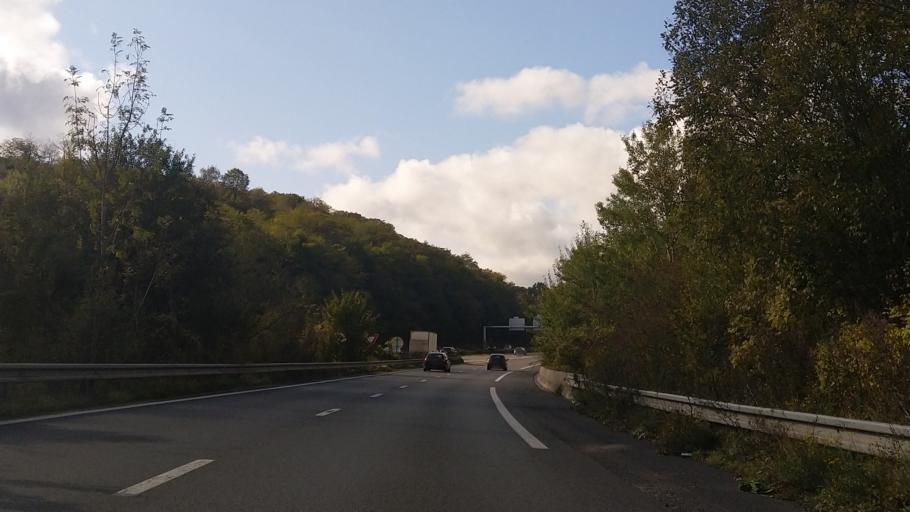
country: FR
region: Ile-de-France
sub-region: Departement du Val-d'Oise
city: Meriel
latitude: 49.0735
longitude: 2.2391
